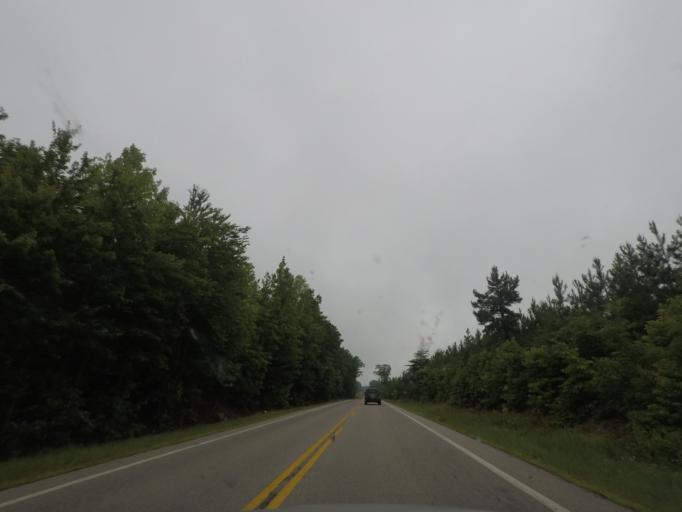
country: US
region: Virginia
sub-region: Prince Edward County
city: Hampden Sydney
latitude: 37.1004
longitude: -78.4721
